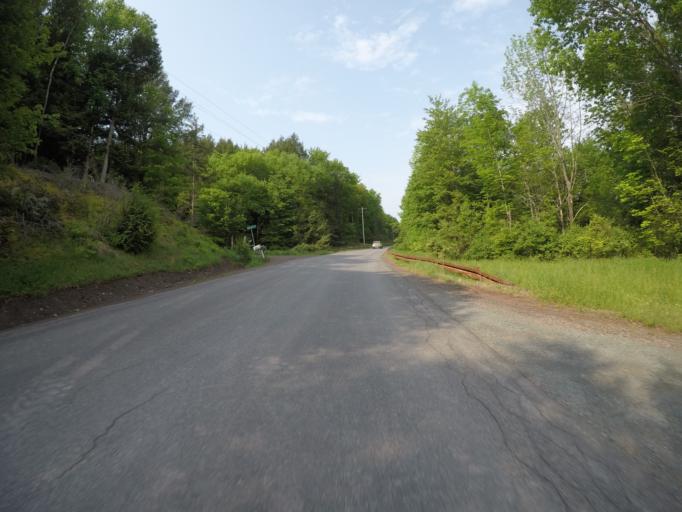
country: US
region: New York
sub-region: Sullivan County
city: Livingston Manor
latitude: 42.1012
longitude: -74.7772
